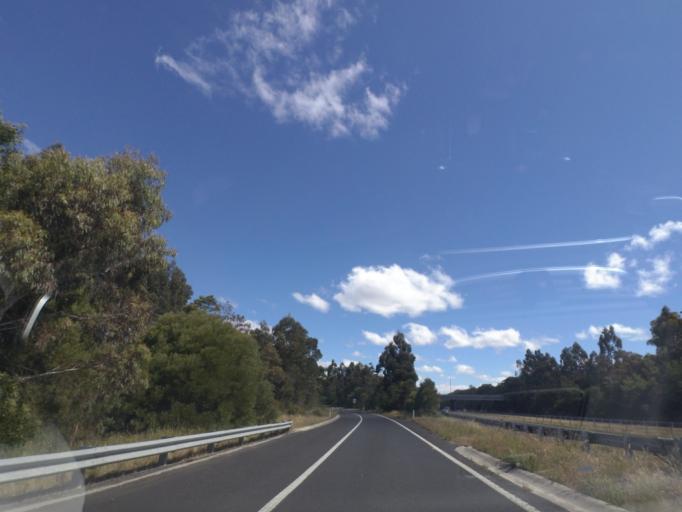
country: AU
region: Victoria
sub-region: Hume
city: Sunbury
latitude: -37.4124
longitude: 144.5451
